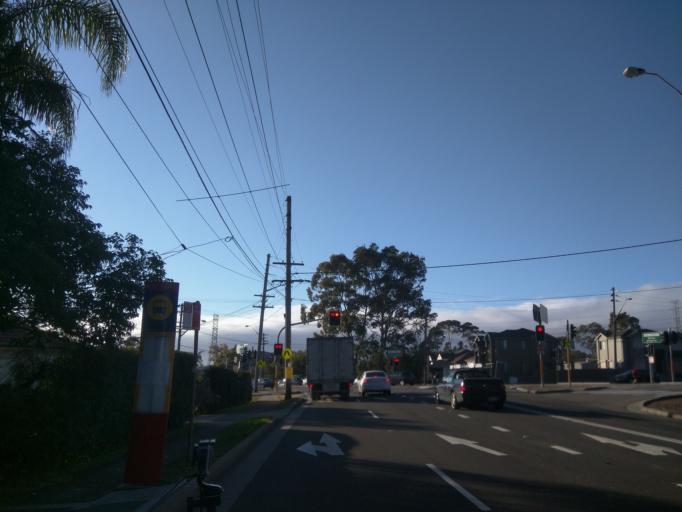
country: AU
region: New South Wales
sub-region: Bankstown
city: Padstow
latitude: -33.9665
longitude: 151.0349
